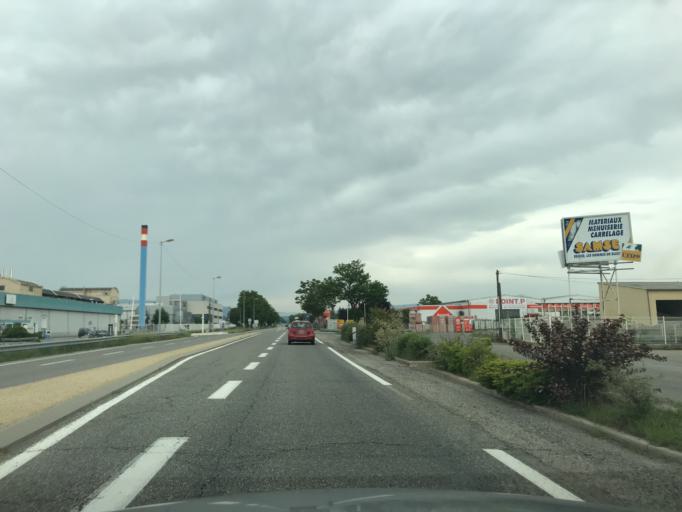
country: FR
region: Provence-Alpes-Cote d'Azur
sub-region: Departement des Alpes-de-Haute-Provence
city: Sisteron
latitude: 44.2062
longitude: 5.9334
